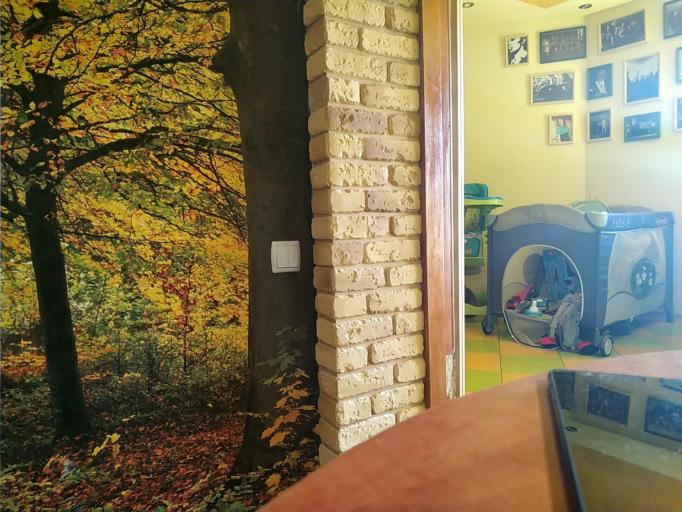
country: RU
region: Tverskaya
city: Vydropuzhsk
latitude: 57.4192
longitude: 34.7728
